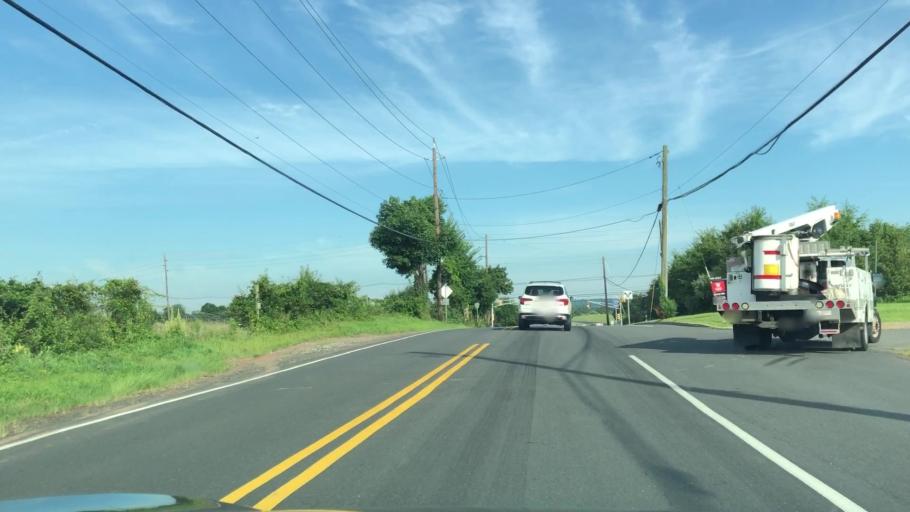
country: US
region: New Jersey
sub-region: Mercer County
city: Pennington
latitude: 40.3386
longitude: -74.7675
